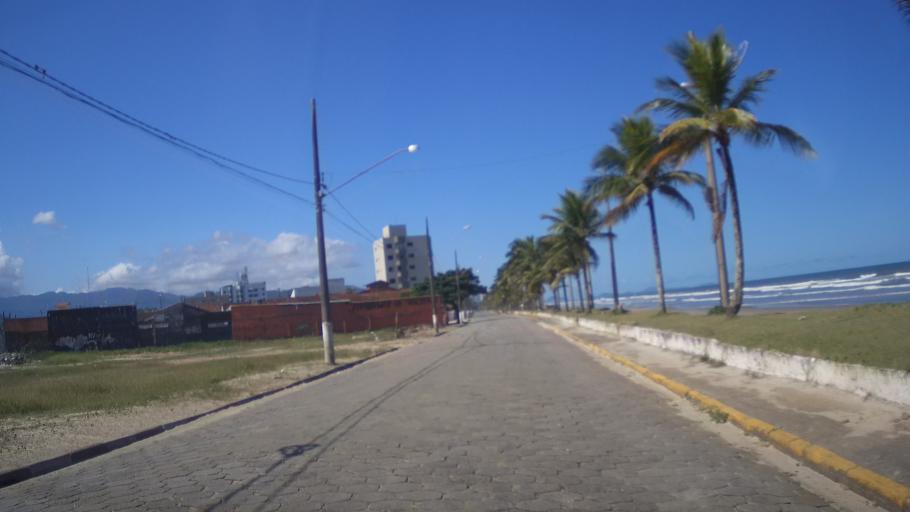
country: BR
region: Sao Paulo
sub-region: Mongagua
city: Mongagua
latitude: -24.1246
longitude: -46.6761
